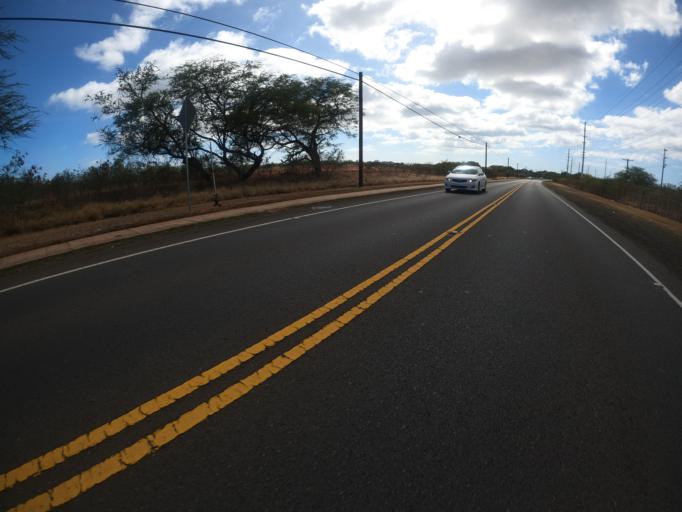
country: US
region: Hawaii
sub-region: Honolulu County
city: Makakilo City
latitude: 21.3238
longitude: -158.0706
